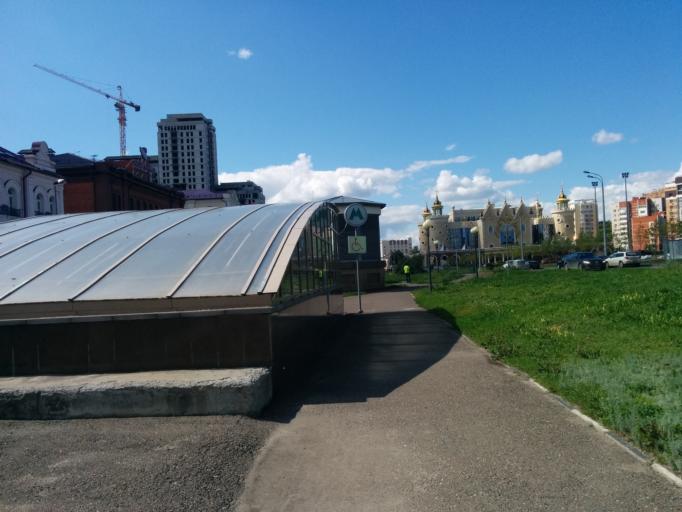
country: RU
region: Tatarstan
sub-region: Gorod Kazan'
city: Kazan
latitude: 55.7777
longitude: 49.1412
